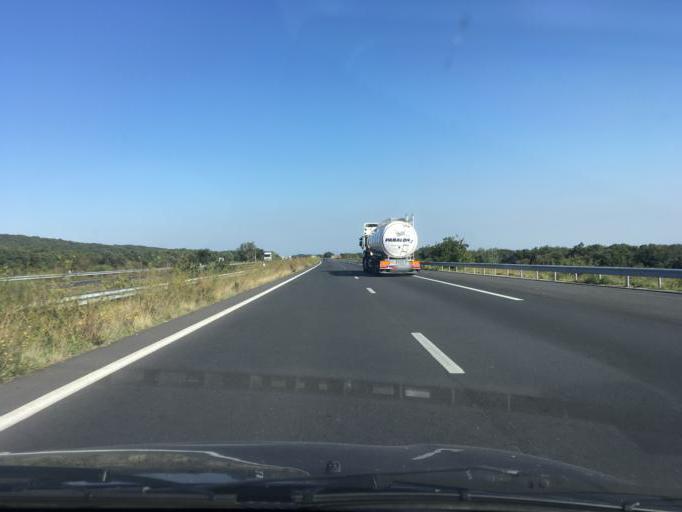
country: FR
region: Languedoc-Roussillon
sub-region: Departement du Gard
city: Rochefort-du-Gard
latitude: 43.9877
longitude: 4.6810
